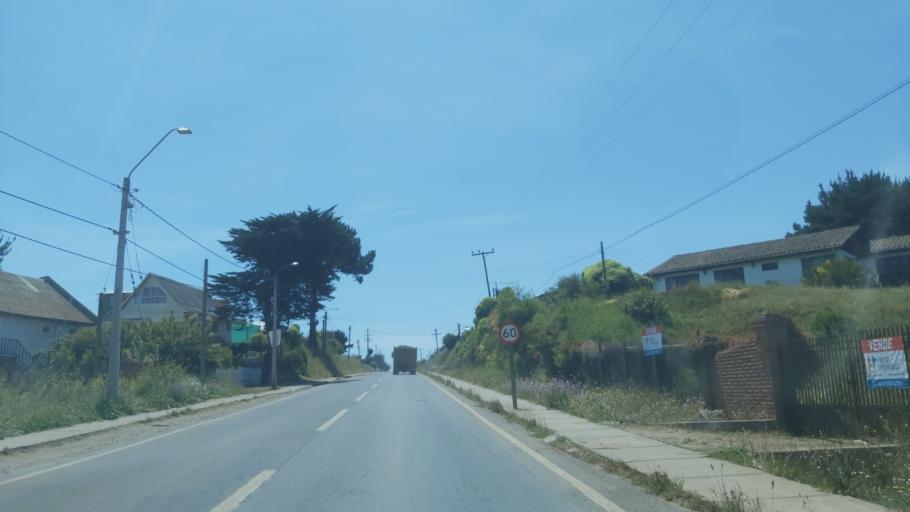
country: CL
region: Maule
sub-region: Provincia de Cauquenes
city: Cauquenes
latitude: -35.8050
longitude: -72.5676
